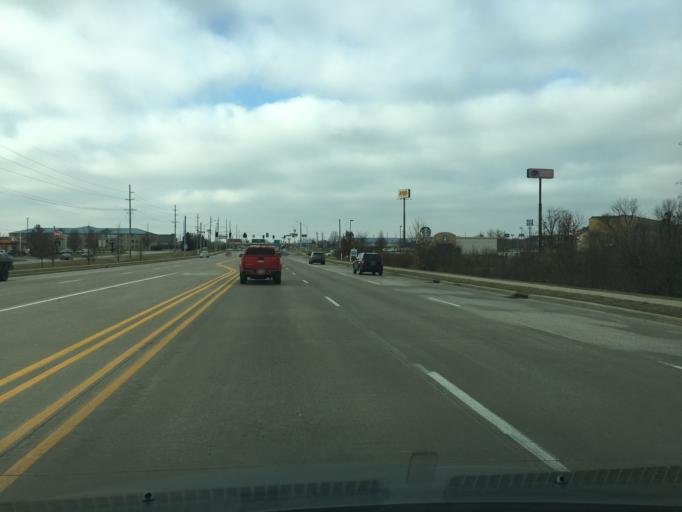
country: US
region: Indiana
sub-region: Tippecanoe County
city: Lafayette
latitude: 40.4176
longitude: -86.8143
